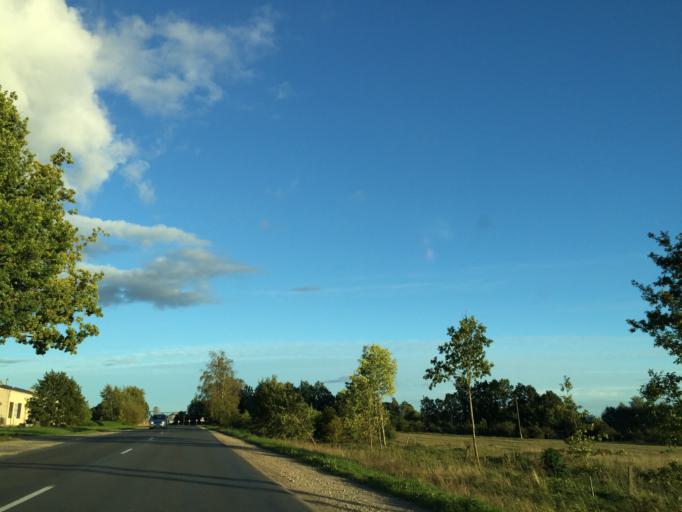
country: LV
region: Saldus Rajons
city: Saldus
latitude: 56.6911
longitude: 22.4497
